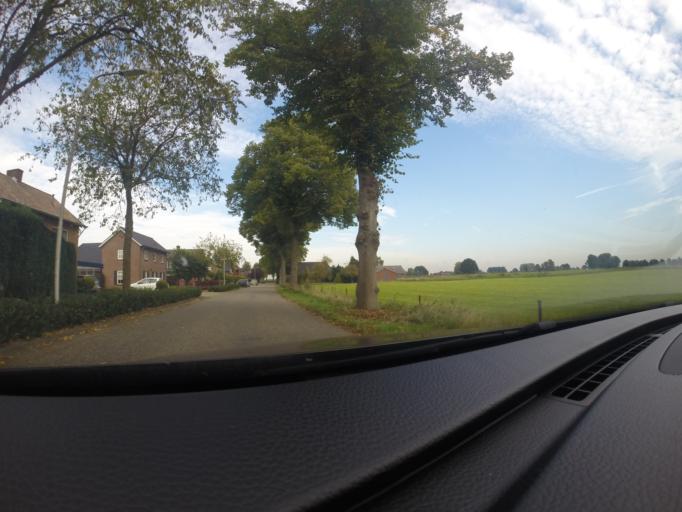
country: NL
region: Gelderland
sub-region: Gemeente Bronckhorst
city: Hengelo
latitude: 52.0256
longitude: 6.2945
